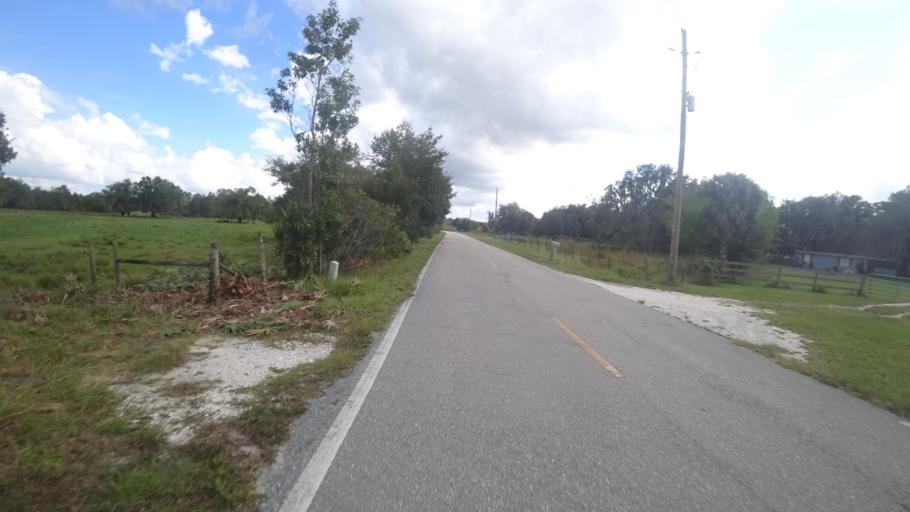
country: US
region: Florida
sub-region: Hillsborough County
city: Wimauma
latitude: 27.6065
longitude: -82.2190
